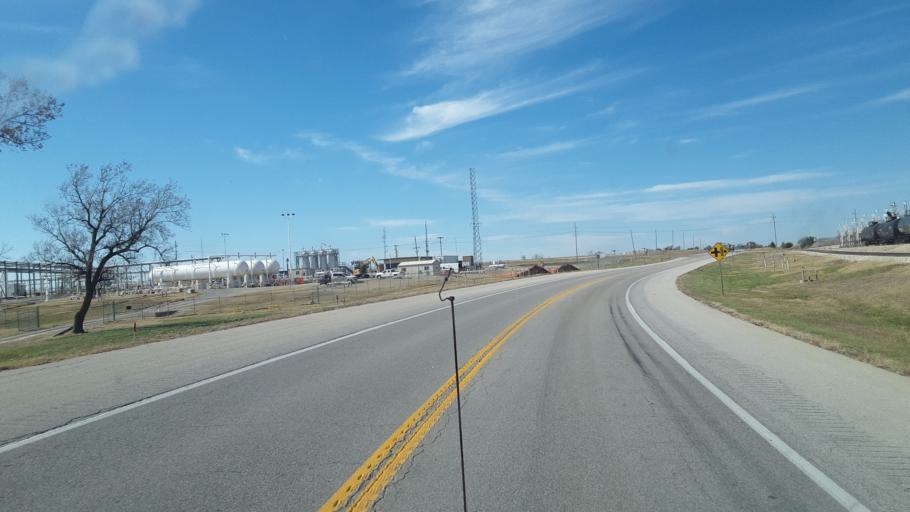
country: US
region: Kansas
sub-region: McPherson County
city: McPherson
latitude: 38.3640
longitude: -97.7744
